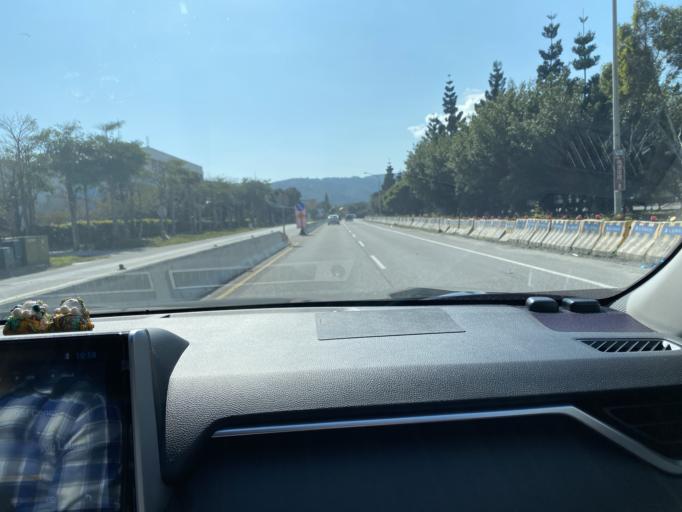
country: TW
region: Taiwan
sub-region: Hualien
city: Hualian
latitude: 23.9336
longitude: 121.5946
